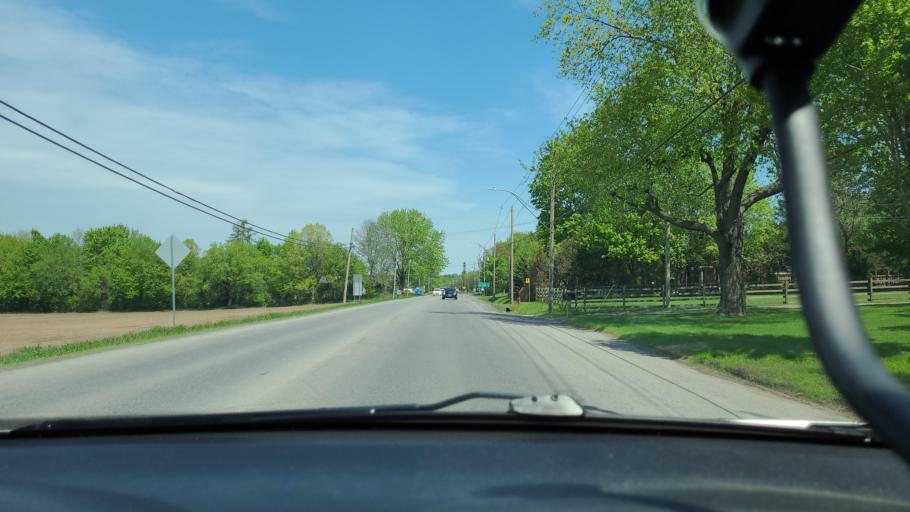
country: CA
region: Quebec
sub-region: Laurentides
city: Lachute
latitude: 45.6601
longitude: -74.3173
